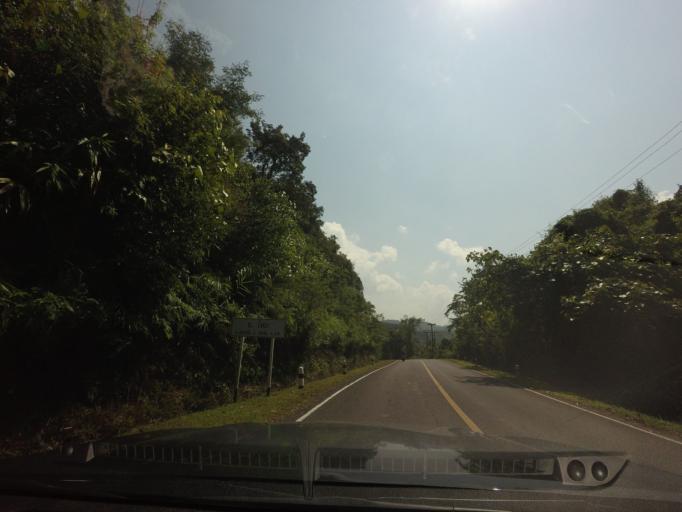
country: TH
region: Nan
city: Bo Kluea
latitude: 19.0645
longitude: 101.1652
